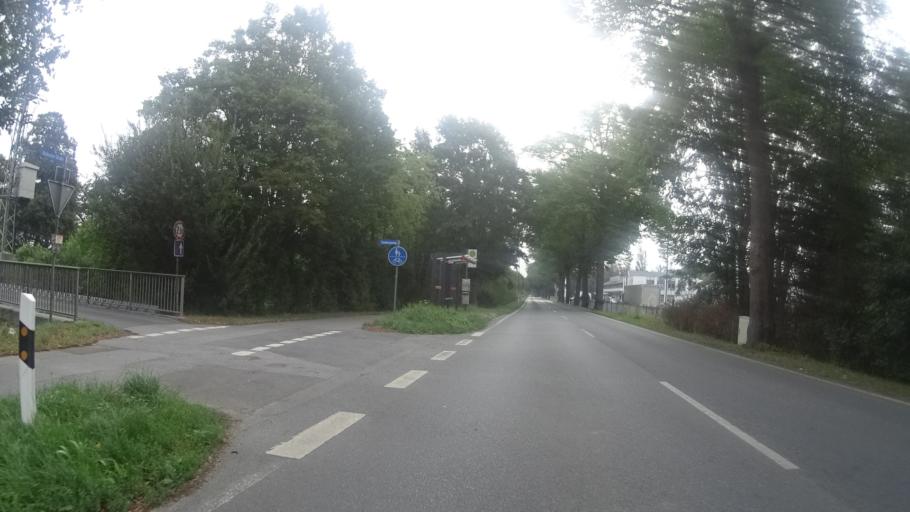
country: DE
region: North Rhine-Westphalia
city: Geldern
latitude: 51.5192
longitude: 6.2959
